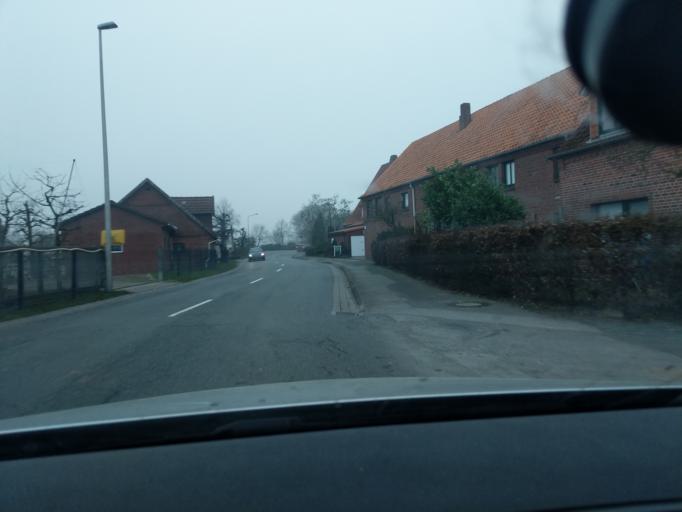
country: DE
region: Lower Saxony
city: Jork
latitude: 53.5496
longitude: 9.6642
